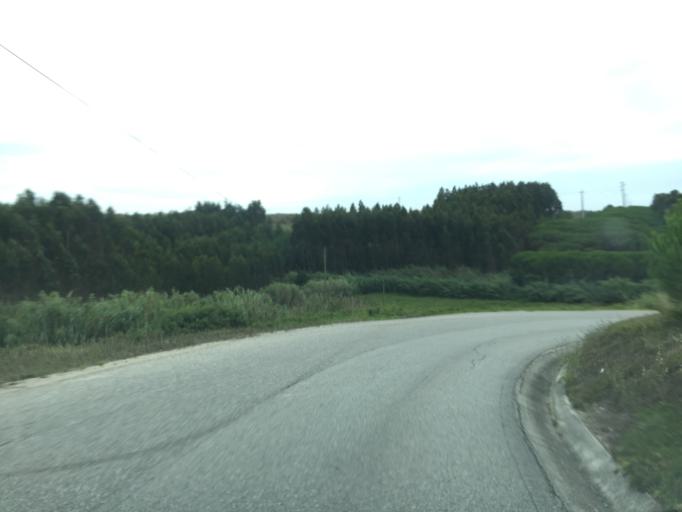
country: PT
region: Leiria
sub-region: Peniche
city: Atouguia da Baleia
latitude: 39.3480
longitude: -9.2938
